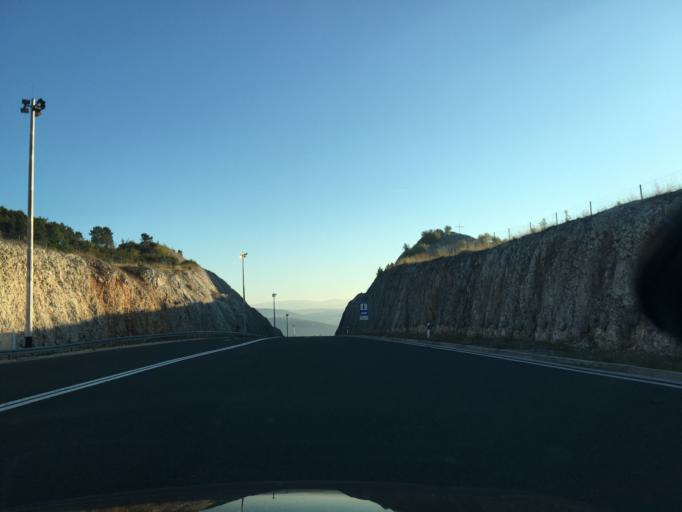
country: HR
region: Splitsko-Dalmatinska
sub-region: Grad Trogir
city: Trogir
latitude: 43.6170
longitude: 16.2363
